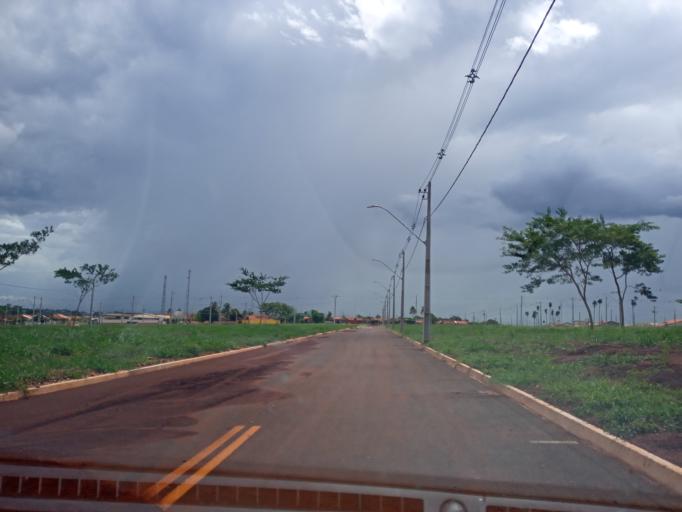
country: BR
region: Goias
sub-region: Itumbiara
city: Itumbiara
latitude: -18.4301
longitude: -49.1815
